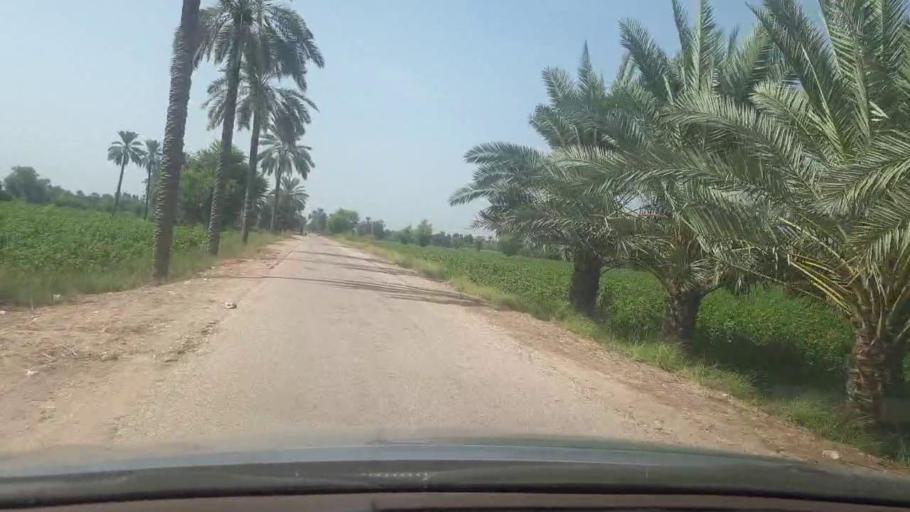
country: PK
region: Sindh
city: Ranipur
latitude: 27.2782
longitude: 68.5816
